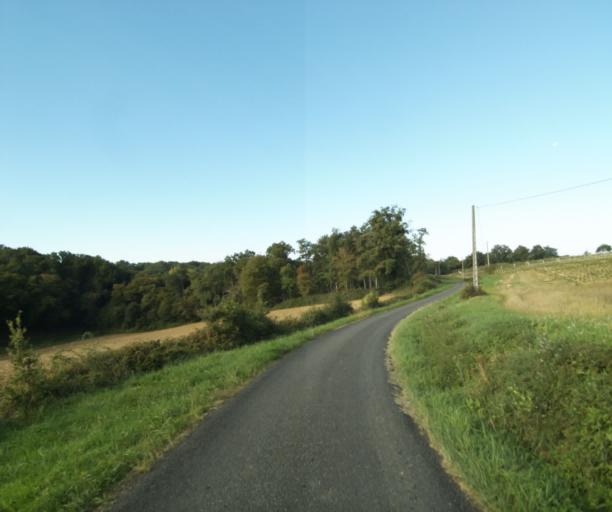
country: FR
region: Midi-Pyrenees
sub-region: Departement du Gers
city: Eauze
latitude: 43.8990
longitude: 0.0244
